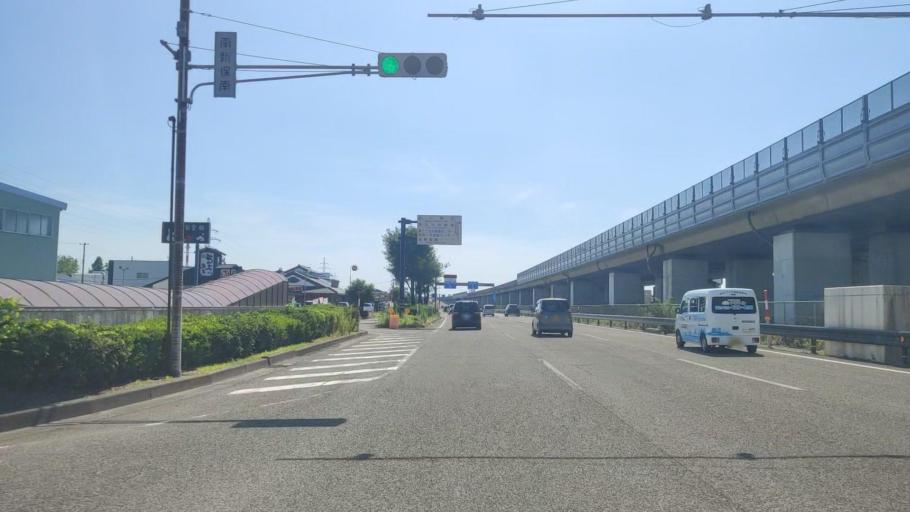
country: JP
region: Ishikawa
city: Kanazawa-shi
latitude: 36.5946
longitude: 136.6368
